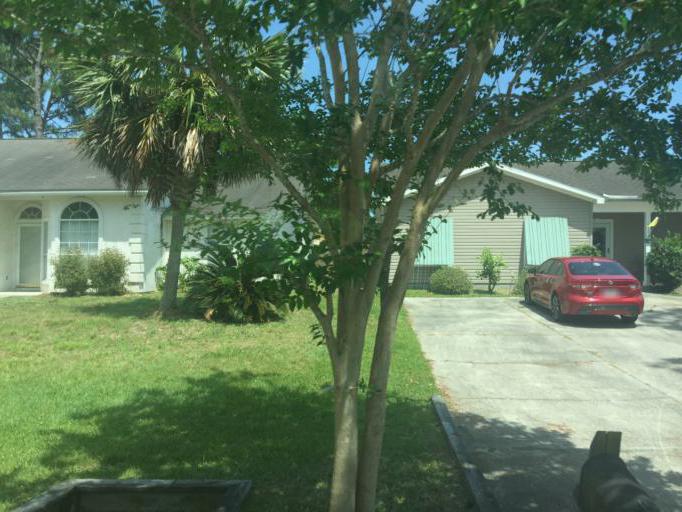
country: US
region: Florida
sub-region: Bay County
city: Laguna Beach
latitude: 30.2391
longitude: -85.9140
